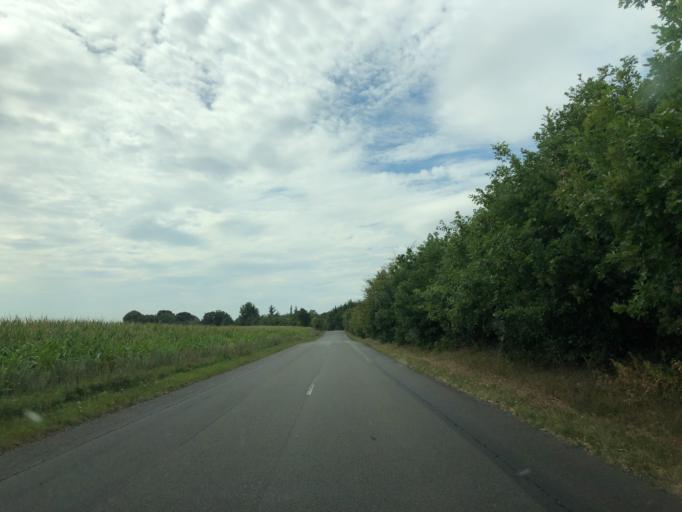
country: DK
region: South Denmark
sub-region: Vejle Kommune
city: Egtved
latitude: 55.6400
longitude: 9.2003
